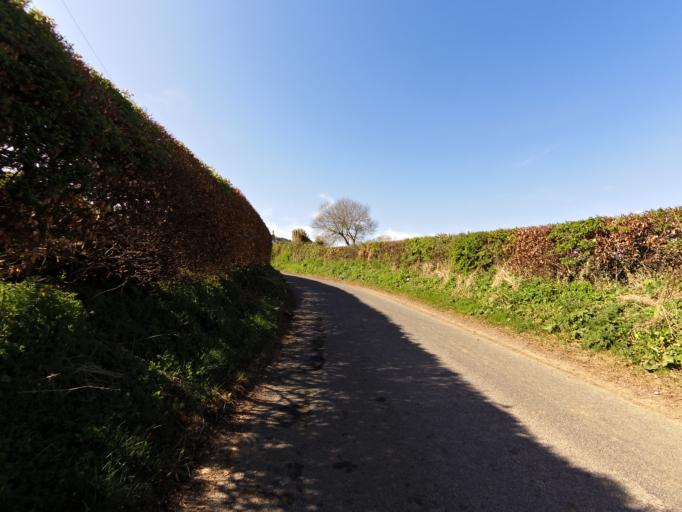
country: GB
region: Scotland
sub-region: Dundee City
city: Dundee
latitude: 56.4072
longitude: -3.0435
